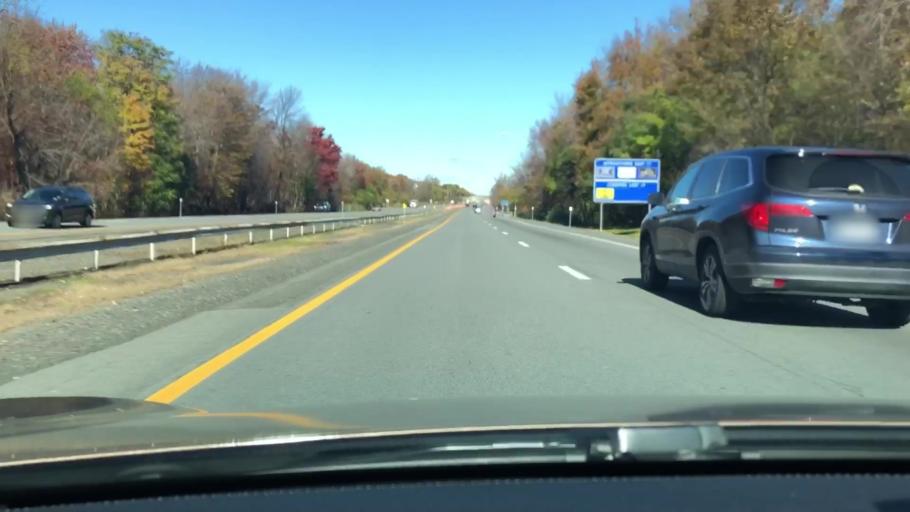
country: US
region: New York
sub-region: Orange County
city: Gardnertown
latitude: 41.4968
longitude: -74.0775
